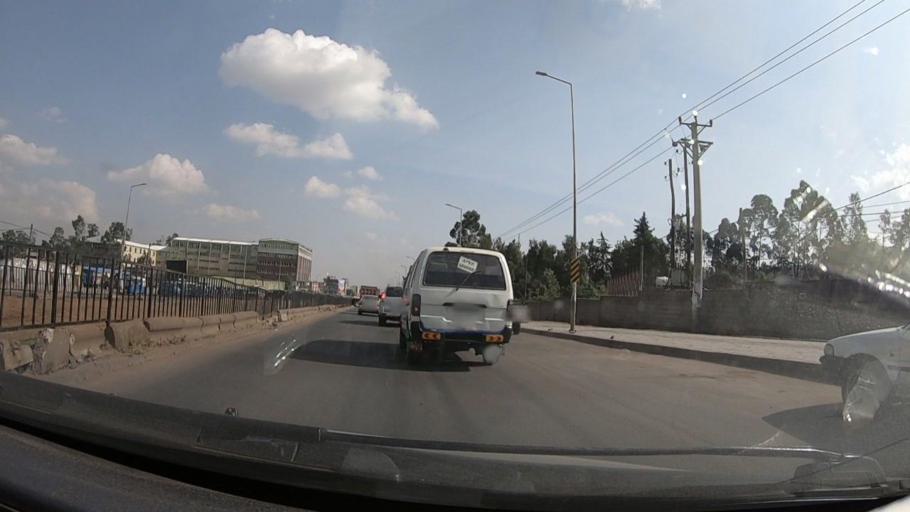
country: ET
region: Adis Abeba
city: Addis Ababa
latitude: 8.9852
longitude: 38.6947
